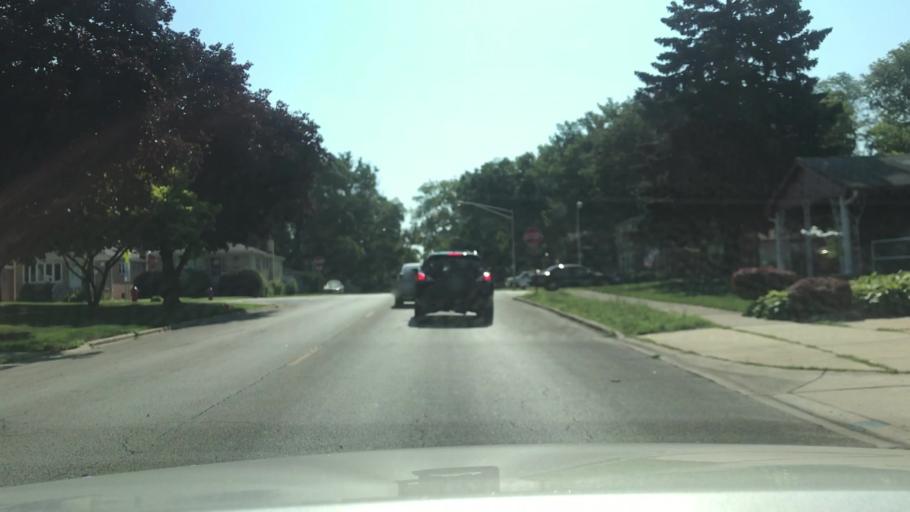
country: US
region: Illinois
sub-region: Cook County
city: Evergreen Park
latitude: 41.7136
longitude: -87.6925
